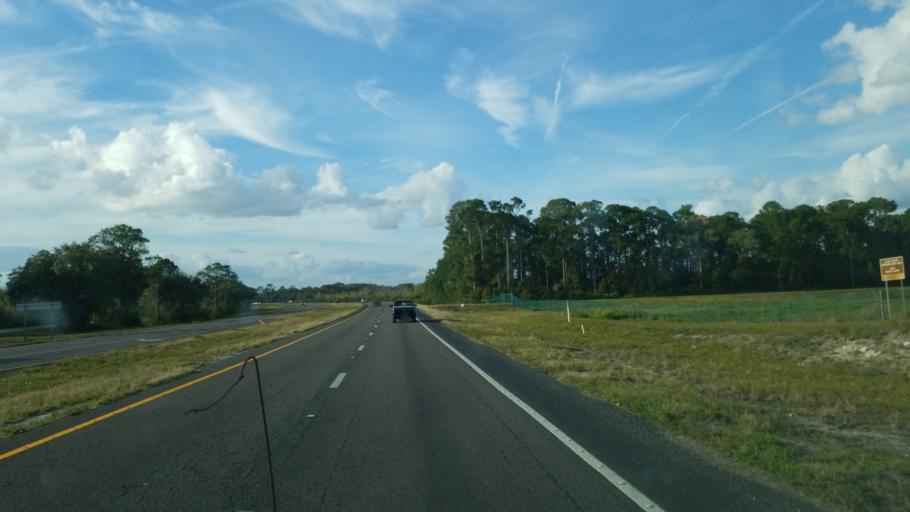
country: US
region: Florida
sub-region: Osceola County
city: Saint Cloud
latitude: 28.2287
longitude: -81.1841
